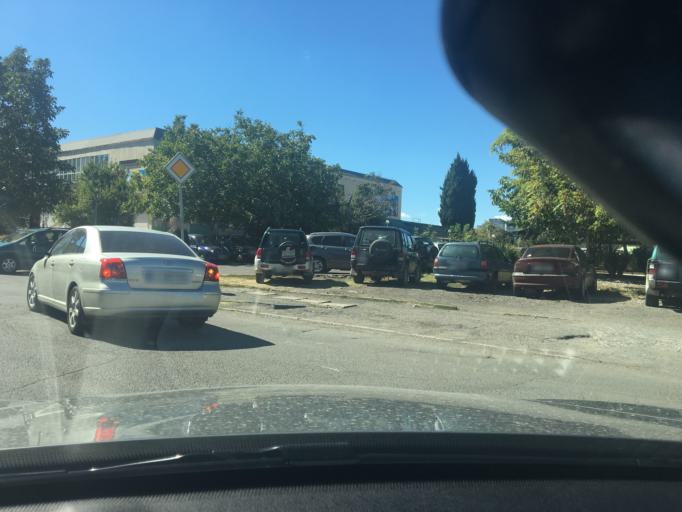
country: BG
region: Burgas
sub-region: Obshtina Burgas
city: Burgas
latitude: 42.5258
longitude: 27.4659
